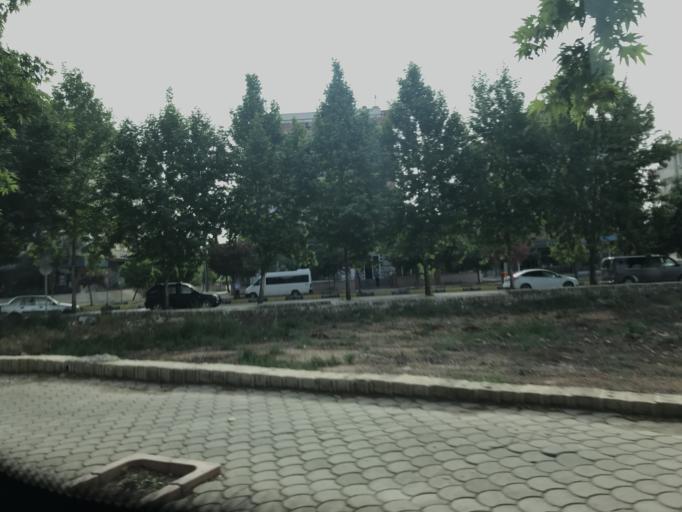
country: TR
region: Gaziantep
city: Sahinbey
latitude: 37.0702
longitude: 37.3390
